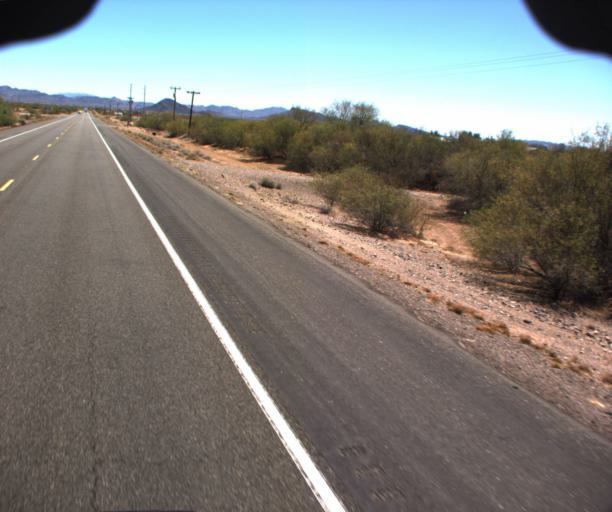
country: US
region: Arizona
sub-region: La Paz County
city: Salome
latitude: 33.7071
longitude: -113.8247
